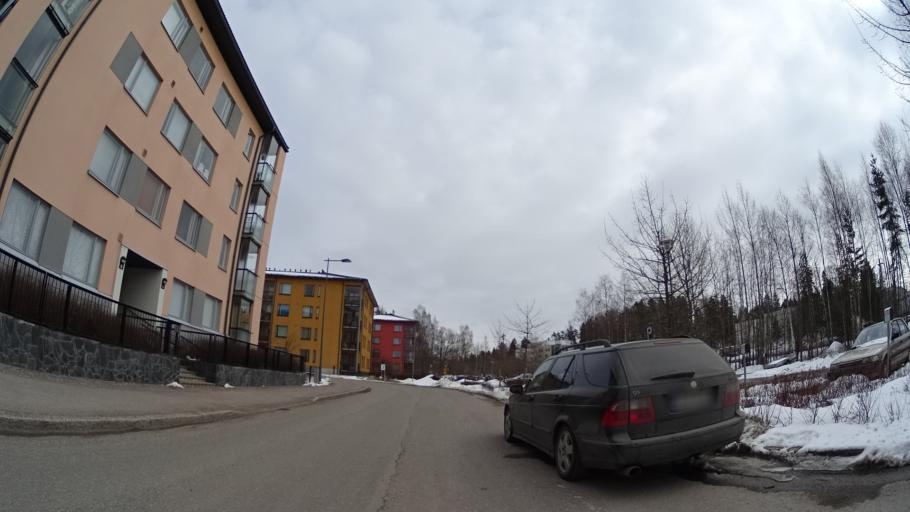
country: FI
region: Uusimaa
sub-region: Helsinki
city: Espoo
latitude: 60.2066
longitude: 24.6834
